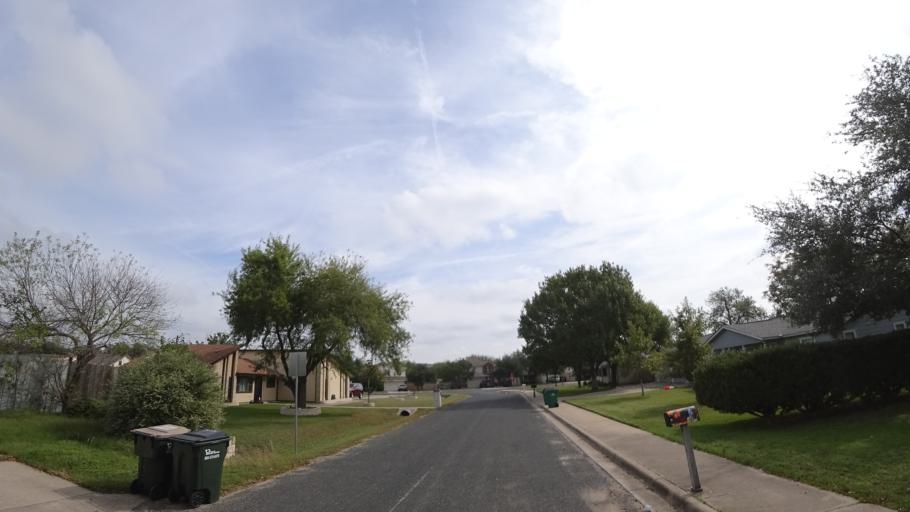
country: US
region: Texas
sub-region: Travis County
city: Windemere
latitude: 30.4452
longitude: -97.6602
